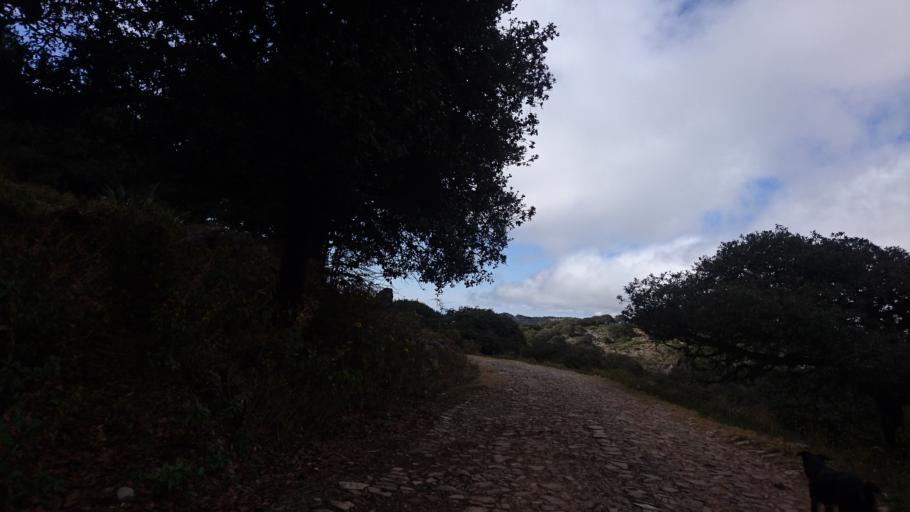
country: MX
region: San Luis Potosi
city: Zaragoza
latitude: 22.0687
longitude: -100.6386
